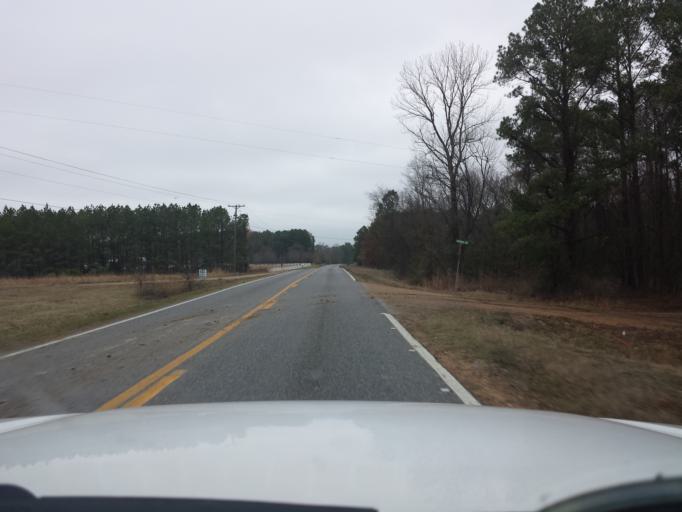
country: US
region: Mississippi
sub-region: Madison County
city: Canton
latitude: 32.4865
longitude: -89.9205
